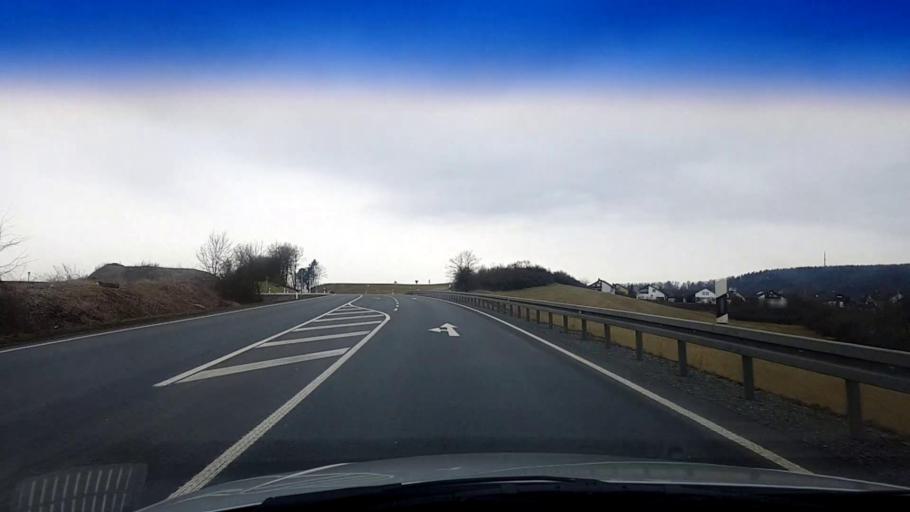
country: DE
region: Bavaria
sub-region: Upper Franconia
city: Kulmbach
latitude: 50.0829
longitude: 11.4630
